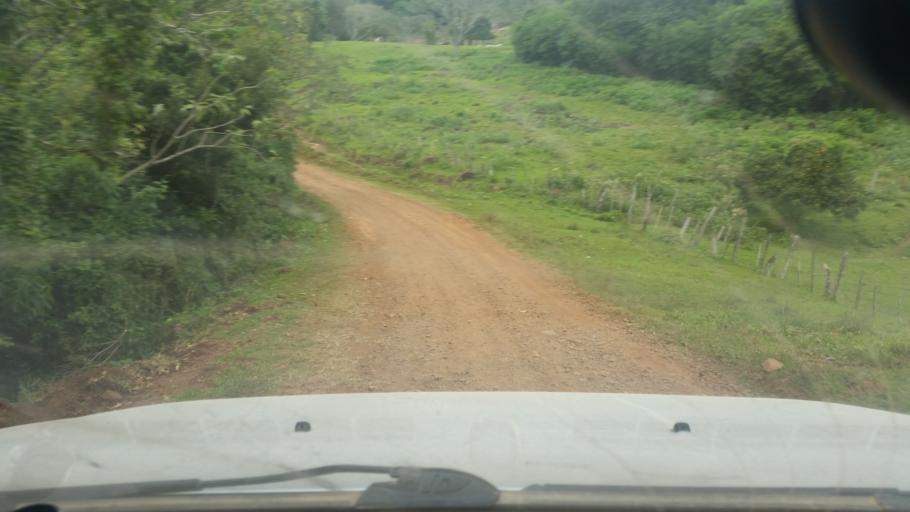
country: PY
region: Guaira
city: Independencia
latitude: -25.8098
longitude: -56.2767
